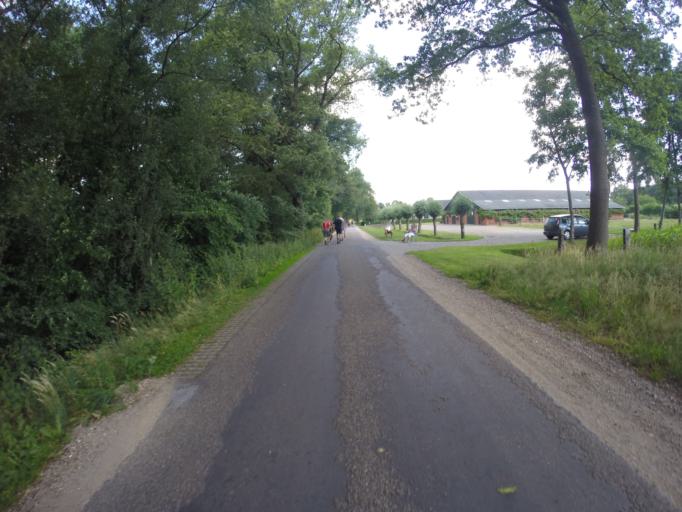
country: NL
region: Gelderland
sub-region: Gemeente Lochem
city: Barchem
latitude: 52.1147
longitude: 6.4349
